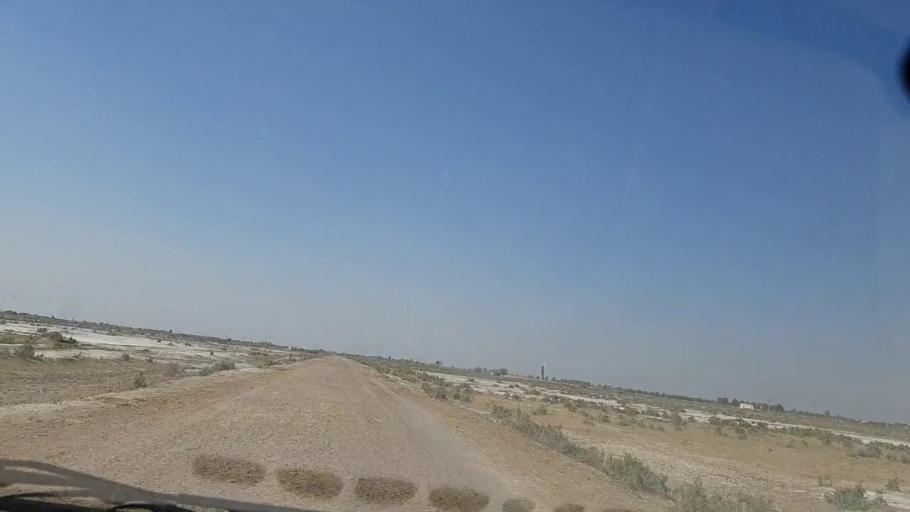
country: PK
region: Sindh
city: Mirwah Gorchani
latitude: 25.3758
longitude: 69.0122
